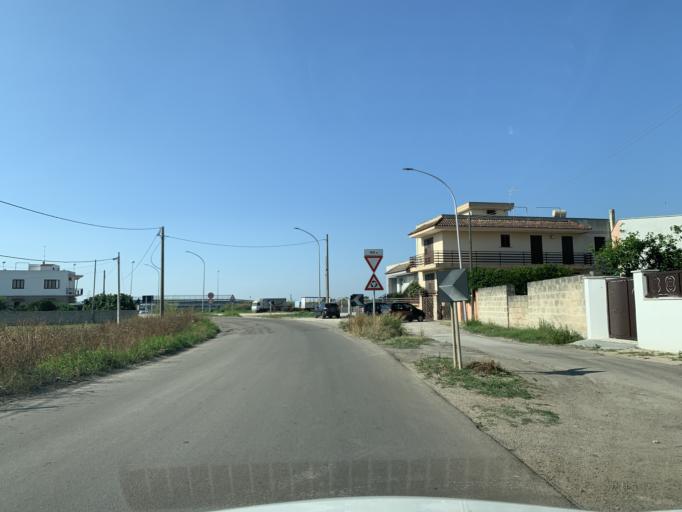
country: IT
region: Apulia
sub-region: Provincia di Lecce
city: Nardo
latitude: 40.1869
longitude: 18.0280
